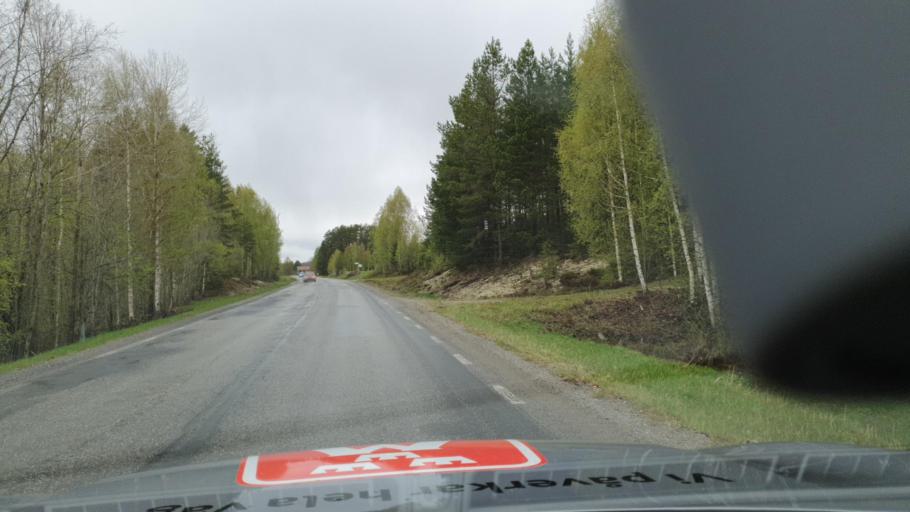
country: SE
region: Vaesternorrland
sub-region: OErnskoeldsviks Kommun
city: Bredbyn
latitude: 63.4653
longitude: 17.9928
